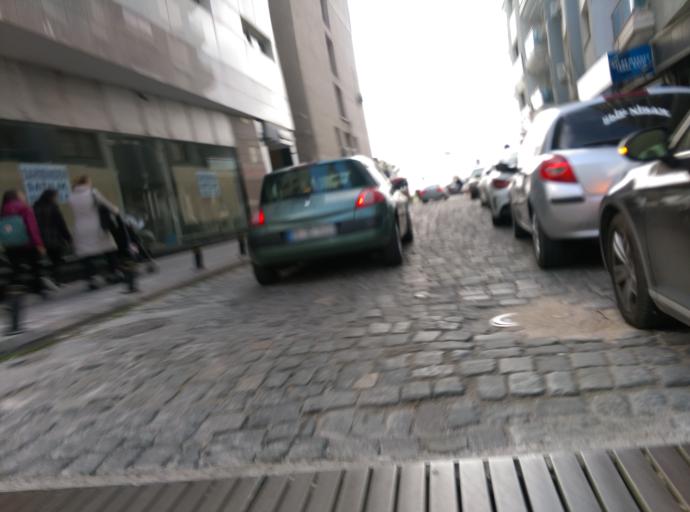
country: TR
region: Izmir
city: Izmir
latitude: 38.4415
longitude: 27.1435
